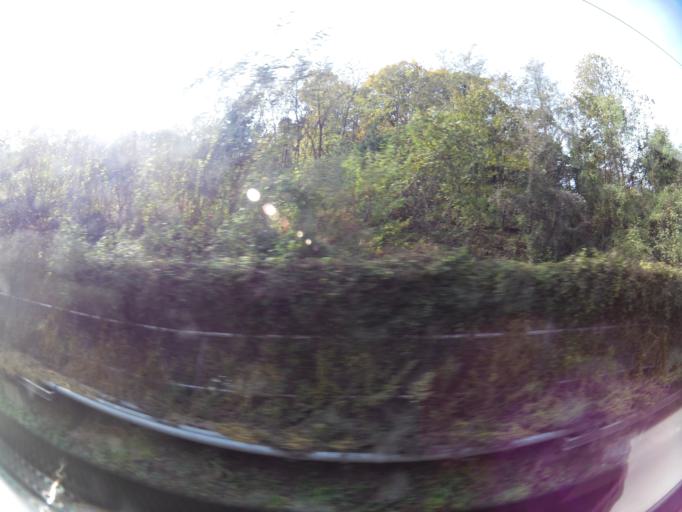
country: KR
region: Daejeon
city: Sintansin
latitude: 36.4658
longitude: 127.4220
